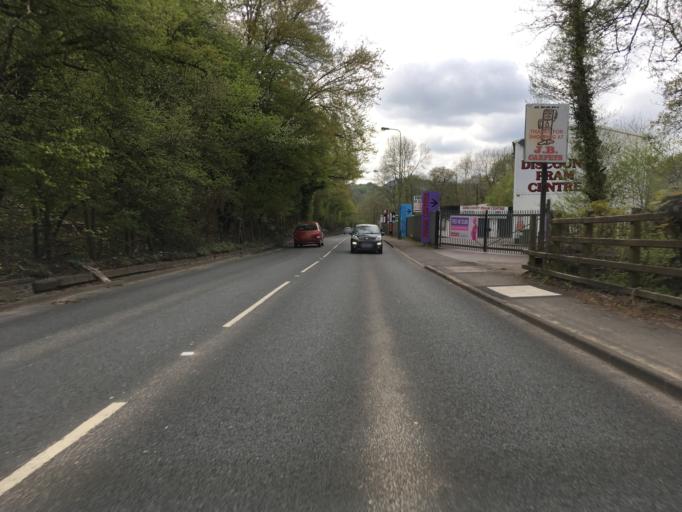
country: GB
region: Wales
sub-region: Merthyr Tydfil County Borough
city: Treharris
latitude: 51.6505
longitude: -3.3048
